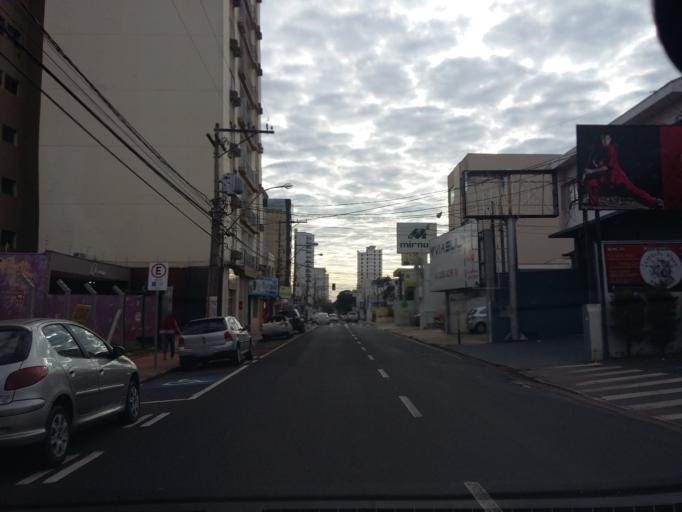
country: BR
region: Sao Paulo
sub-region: Sao Jose Do Rio Preto
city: Sao Jose do Rio Preto
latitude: -20.8199
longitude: -49.3897
